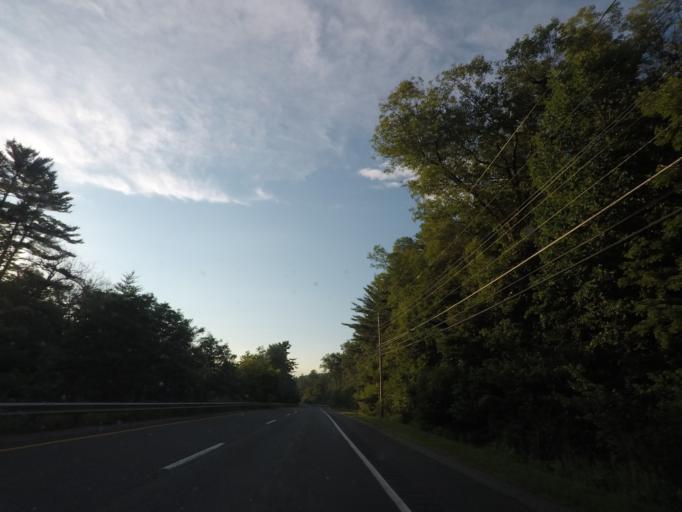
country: US
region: Massachusetts
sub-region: Hampden County
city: Brimfield
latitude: 42.1285
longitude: -72.2536
